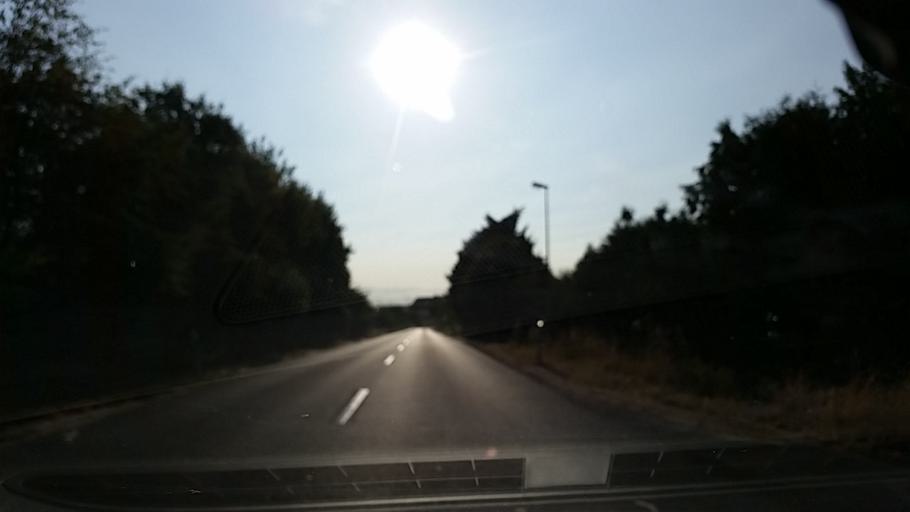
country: DE
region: Lower Saxony
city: Lehre
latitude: 52.2961
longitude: 10.7157
